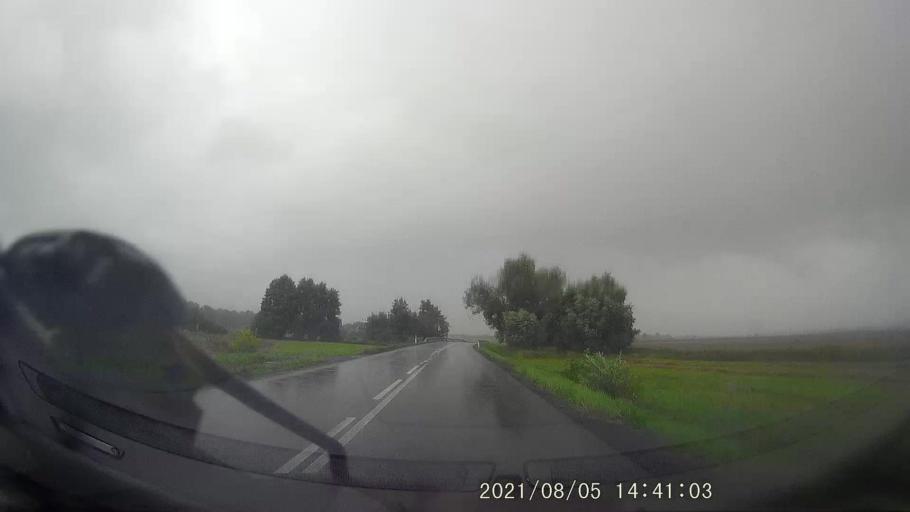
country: PL
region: Opole Voivodeship
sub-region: Powiat nyski
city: Nysa
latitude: 50.4710
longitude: 17.4206
